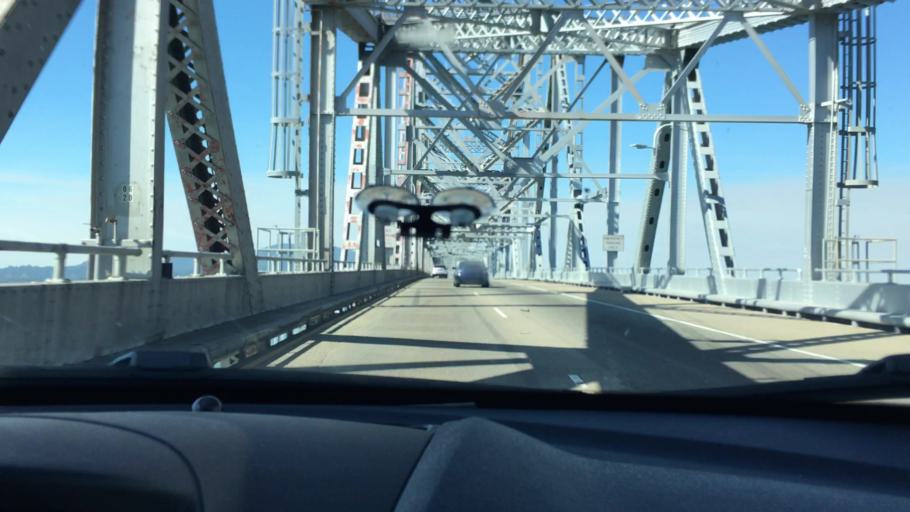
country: US
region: California
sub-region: Marin County
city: Tiburon
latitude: 37.9349
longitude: -122.4417
